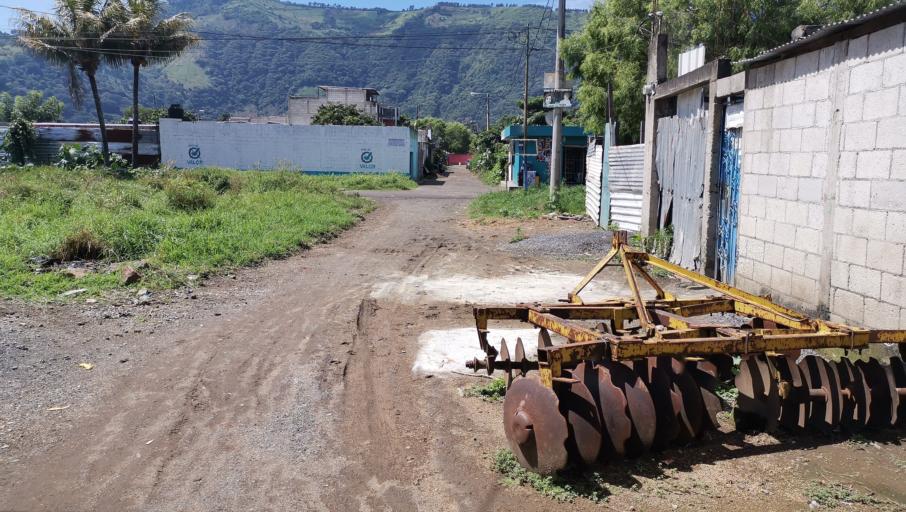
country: GT
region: Escuintla
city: San Vicente Pacaya
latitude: 14.4450
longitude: -90.6329
